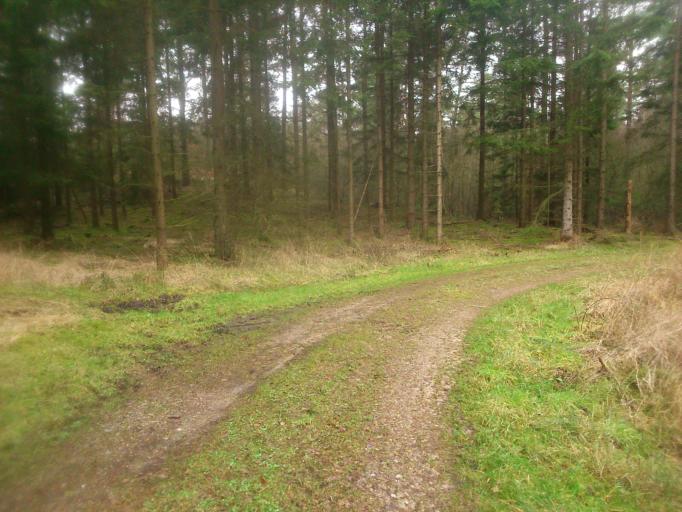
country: DK
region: Central Jutland
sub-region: Viborg Kommune
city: Bjerringbro
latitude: 56.3906
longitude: 9.7172
